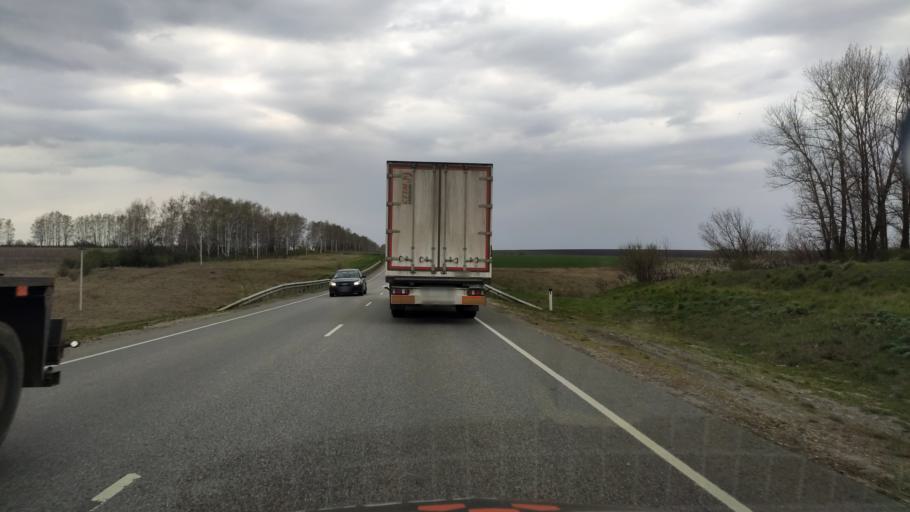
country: RU
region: Kursk
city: Gorshechnoye
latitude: 51.5488
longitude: 38.1230
